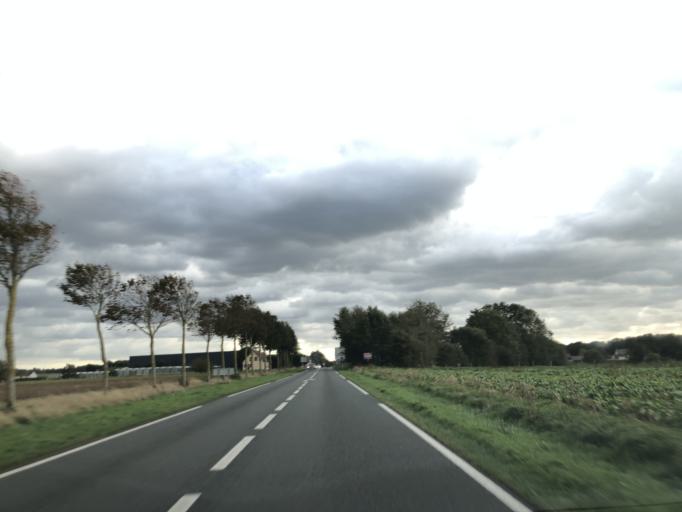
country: FR
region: Picardie
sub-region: Departement de la Somme
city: Ault
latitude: 50.0980
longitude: 1.4667
